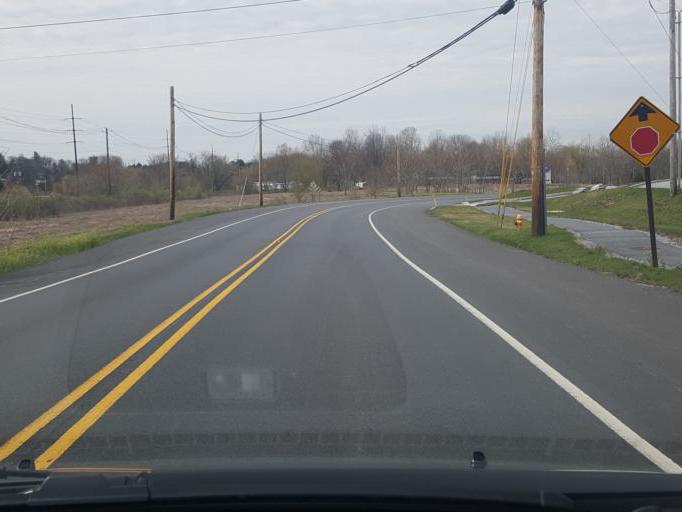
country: US
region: Pennsylvania
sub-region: Dauphin County
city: Hummelstown
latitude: 40.2725
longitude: -76.6864
